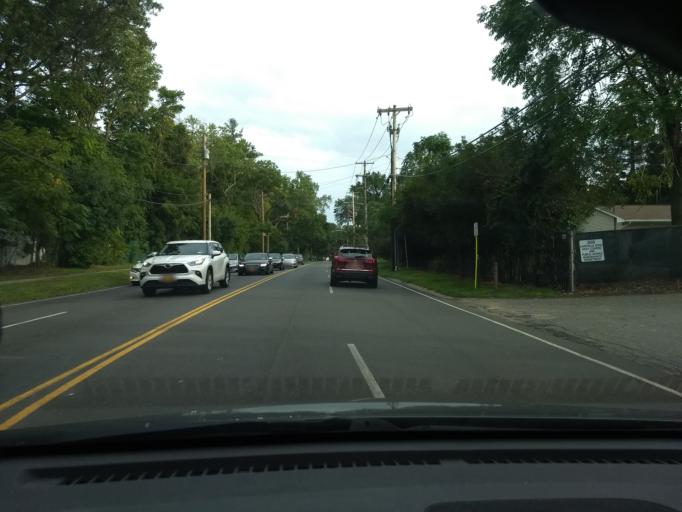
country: US
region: New York
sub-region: Nassau County
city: Lake Success
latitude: 40.7686
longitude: -73.7079
